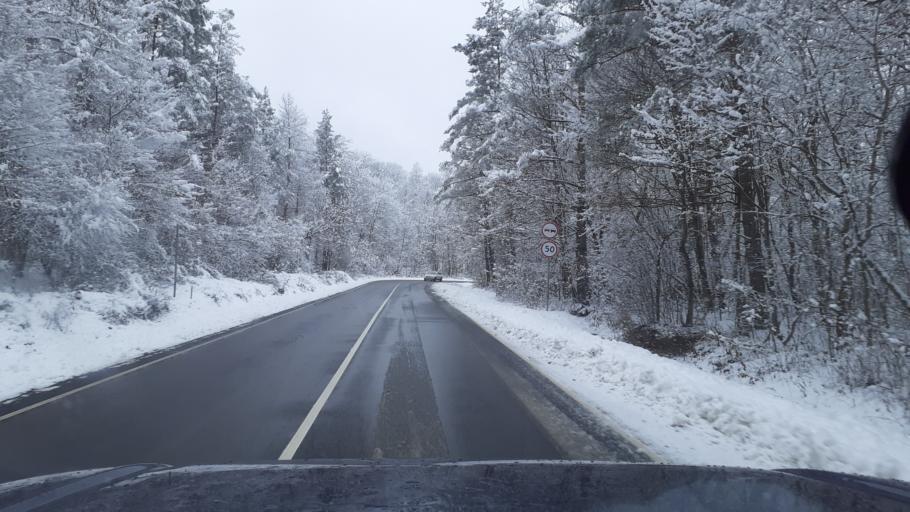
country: RU
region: Adygeya
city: Kamennomostskiy
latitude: 44.1842
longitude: 40.1609
